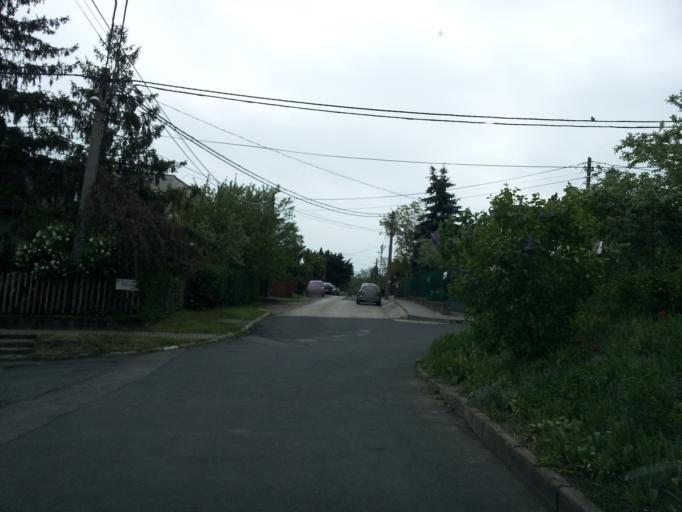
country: HU
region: Budapest
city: Budapest XXII. keruelet
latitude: 47.4415
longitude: 19.0176
